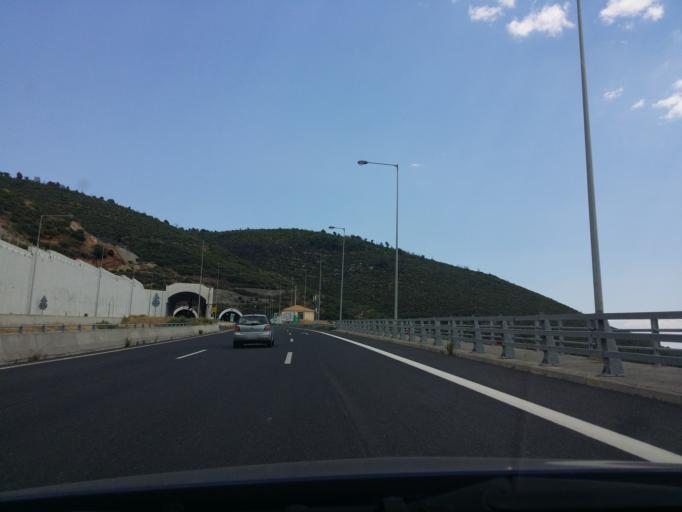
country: GR
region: Peloponnese
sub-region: Nomos Arkadias
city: Megalopoli
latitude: 37.3861
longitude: 22.1933
